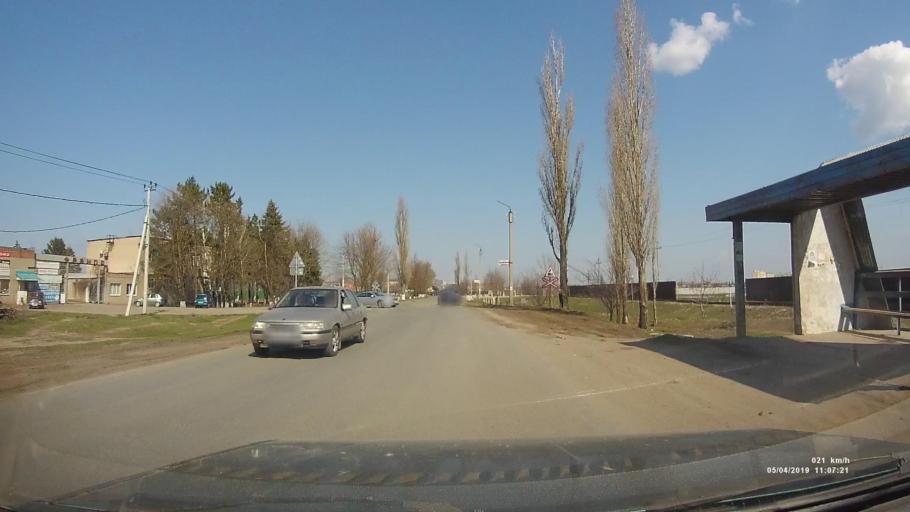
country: RU
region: Rostov
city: Azov
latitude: 47.0810
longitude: 39.4374
